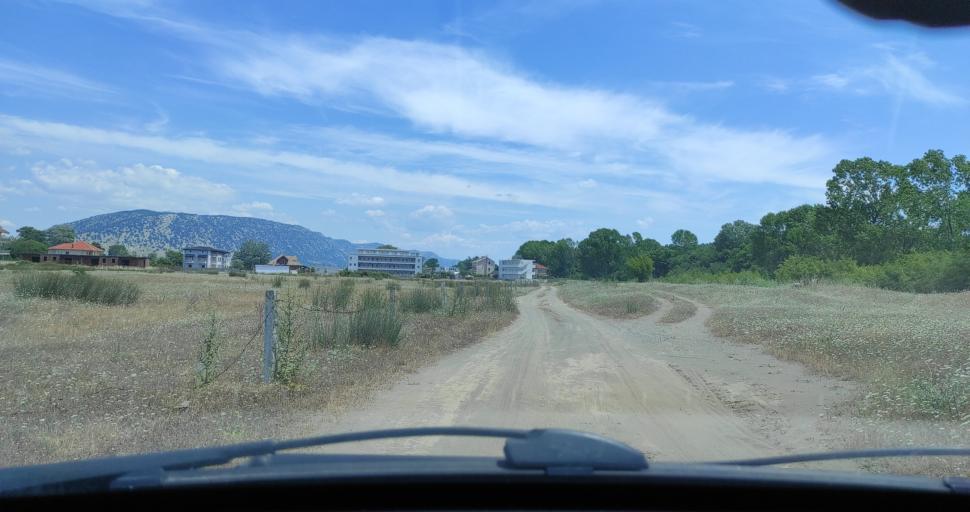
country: AL
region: Shkoder
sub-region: Rrethi i Shkodres
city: Velipoje
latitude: 41.8694
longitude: 19.3972
